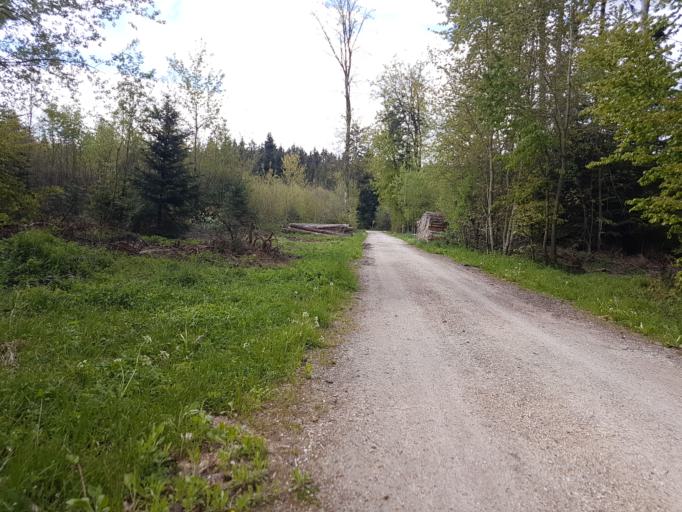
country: CH
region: Aargau
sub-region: Bezirk Zofingen
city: Fulenbach
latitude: 47.2920
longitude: 7.8467
